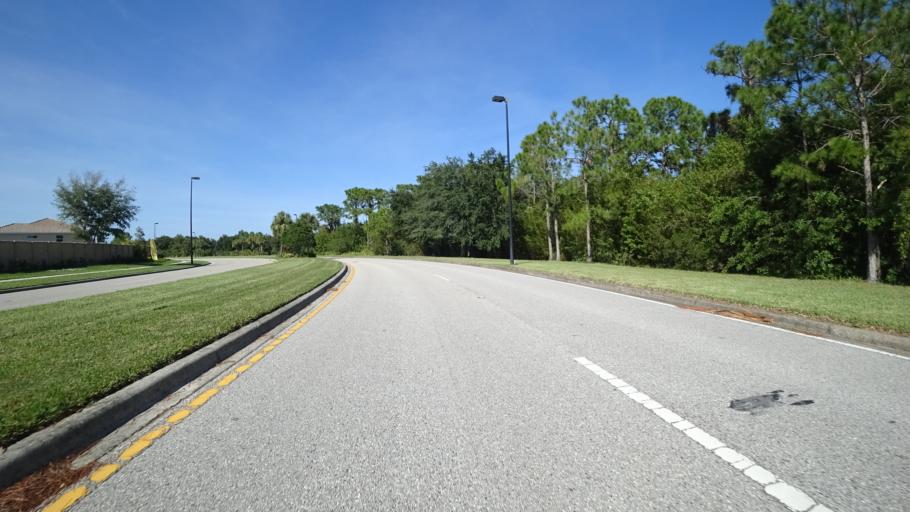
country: US
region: Florida
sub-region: Sarasota County
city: The Meadows
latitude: 27.3999
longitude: -82.4473
